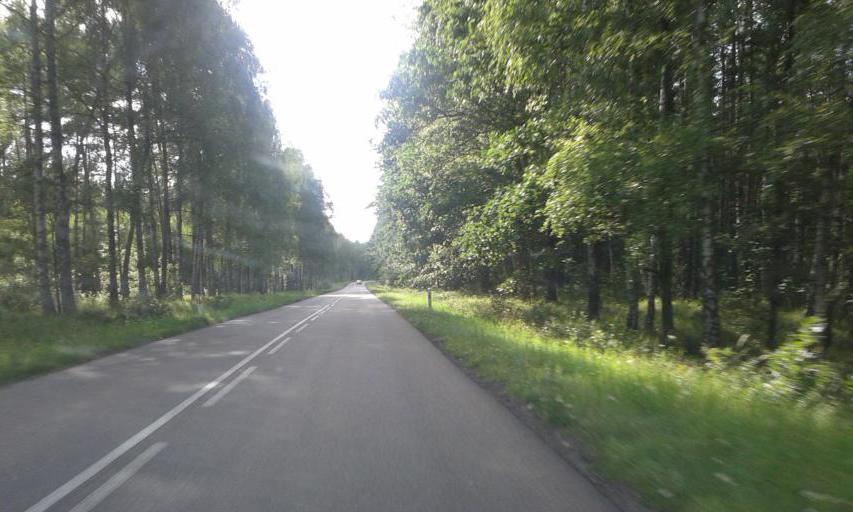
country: PL
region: West Pomeranian Voivodeship
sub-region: Powiat szczecinecki
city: Barwice
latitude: 53.7550
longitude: 16.2683
